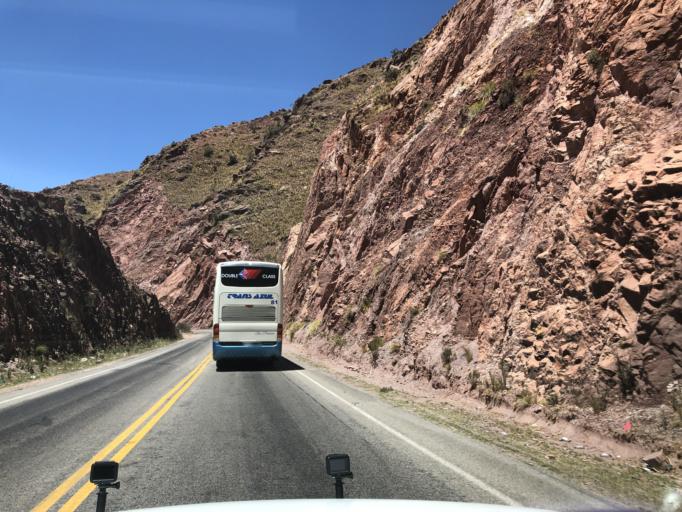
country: BO
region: Cochabamba
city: Irpa Irpa
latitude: -17.7228
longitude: -66.6151
